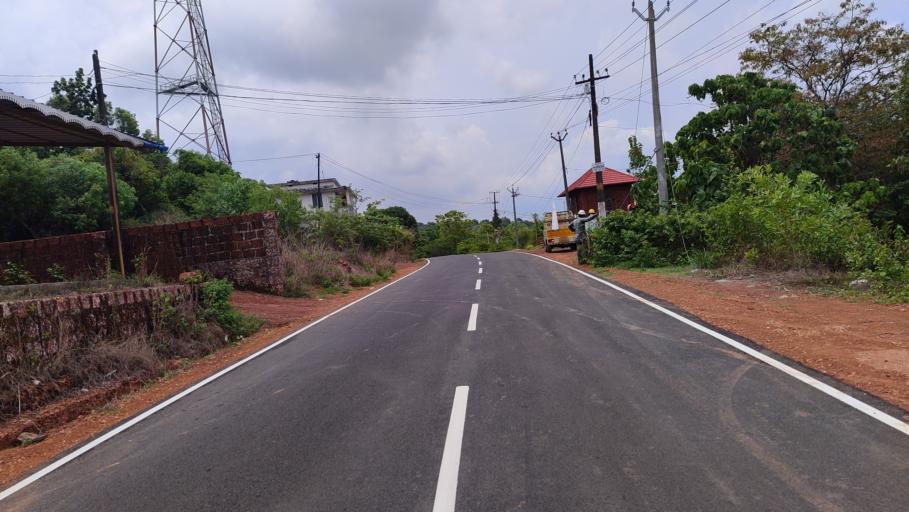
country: IN
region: Kerala
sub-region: Kasaragod District
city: Kannangad
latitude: 12.3176
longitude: 75.1472
